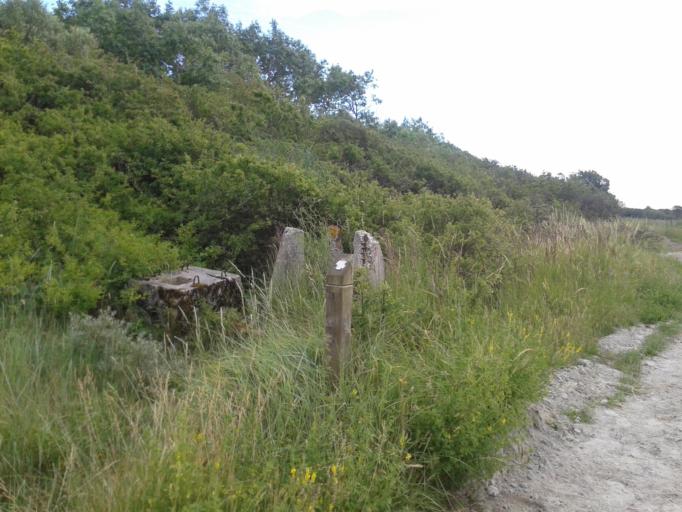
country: FR
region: Picardie
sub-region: Departement de la Somme
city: Fort-Mahon-Plage
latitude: 50.3579
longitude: 1.5659
